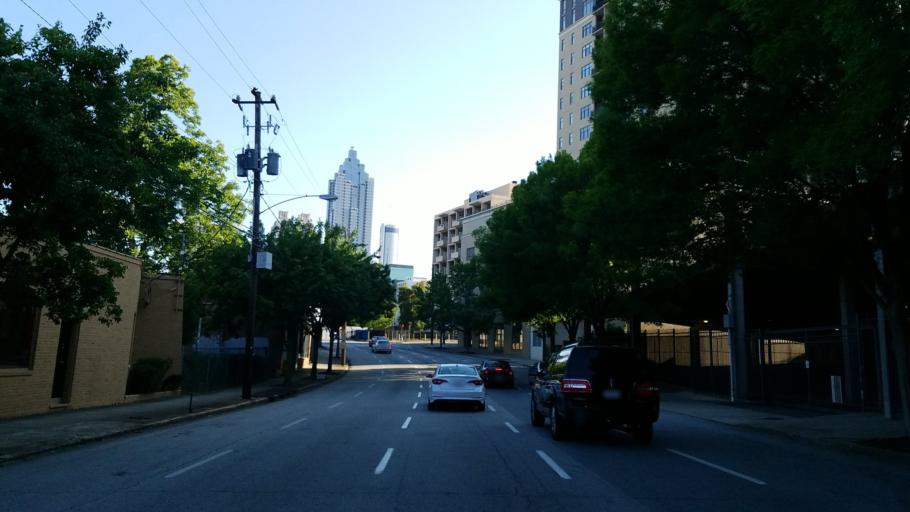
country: US
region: Georgia
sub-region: Fulton County
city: Atlanta
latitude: 33.7708
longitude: -84.3837
